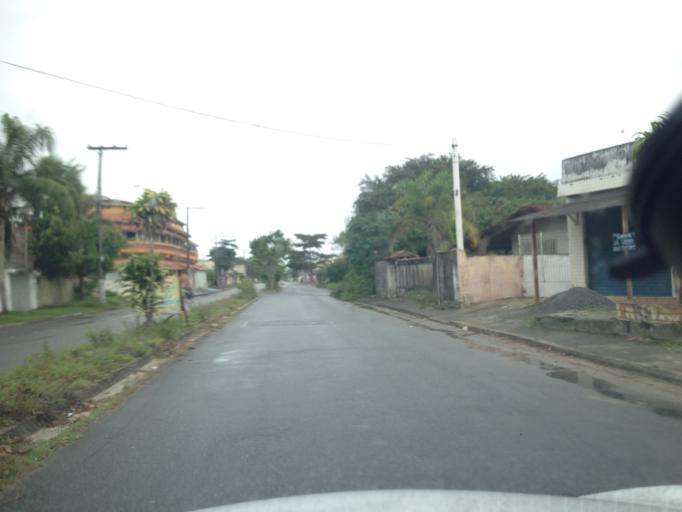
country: BR
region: Sao Paulo
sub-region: Itanhaem
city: Itanhaem
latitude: -24.2329
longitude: -46.8785
